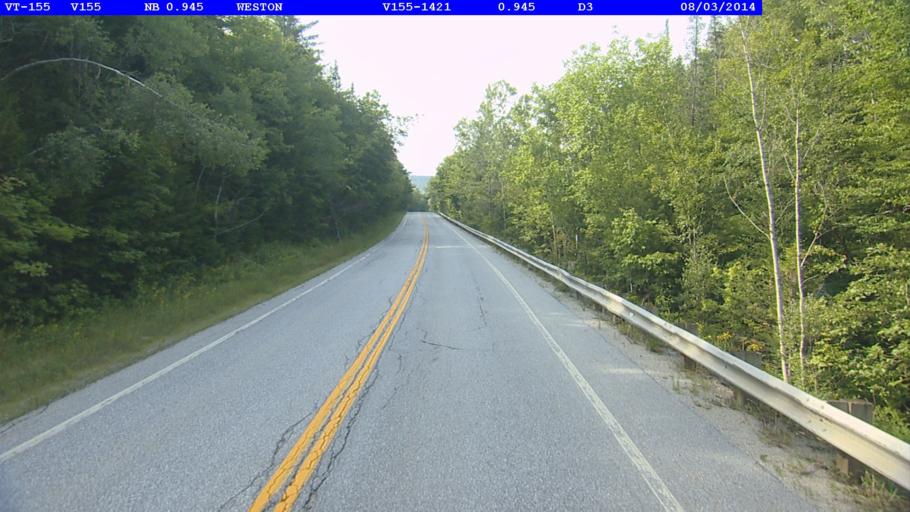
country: US
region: Vermont
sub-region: Windsor County
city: Chester
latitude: 43.3496
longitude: -72.7915
